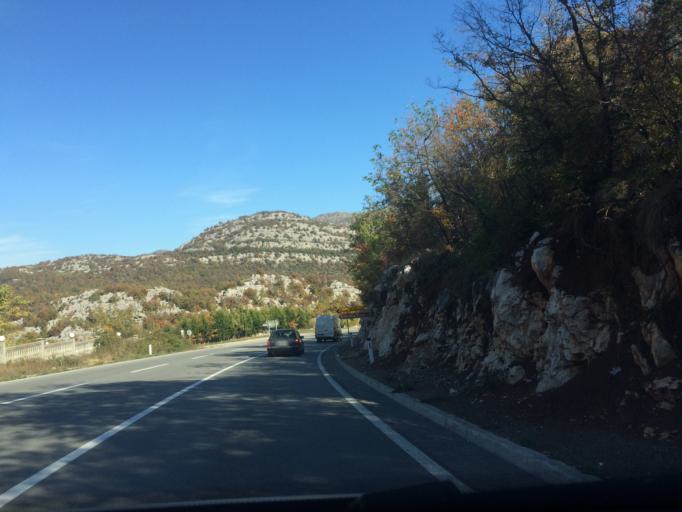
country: ME
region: Cetinje
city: Cetinje
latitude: 42.3850
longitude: 19.0554
